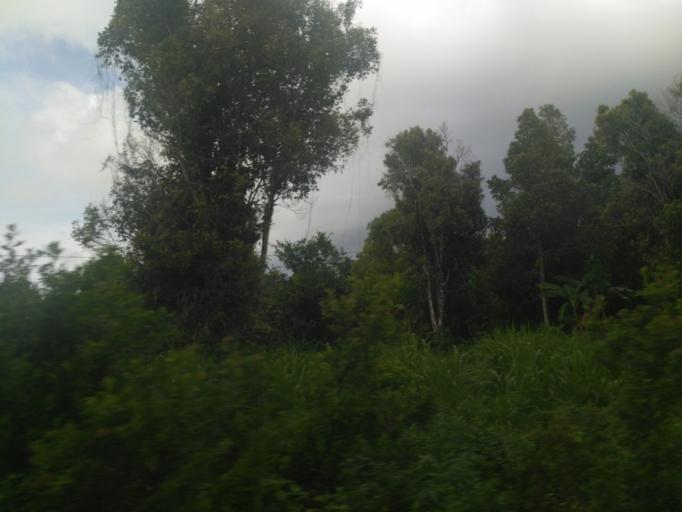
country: TZ
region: Zanzibar Central/South
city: Koani
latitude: -6.1083
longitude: 39.2854
